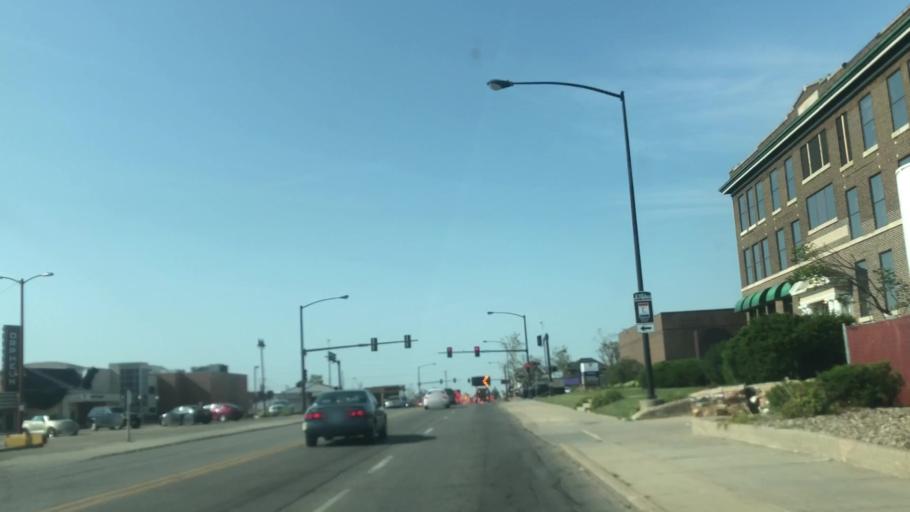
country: US
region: Iowa
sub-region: Marshall County
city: Marshalltown
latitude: 42.0483
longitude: -92.9079
